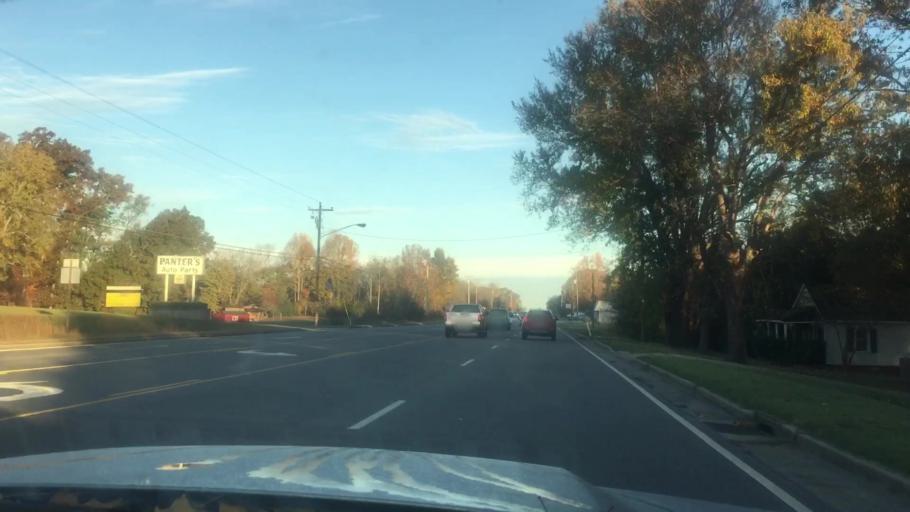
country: US
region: Tennessee
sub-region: Franklin County
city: Estill Springs
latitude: 35.2824
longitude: -86.1388
